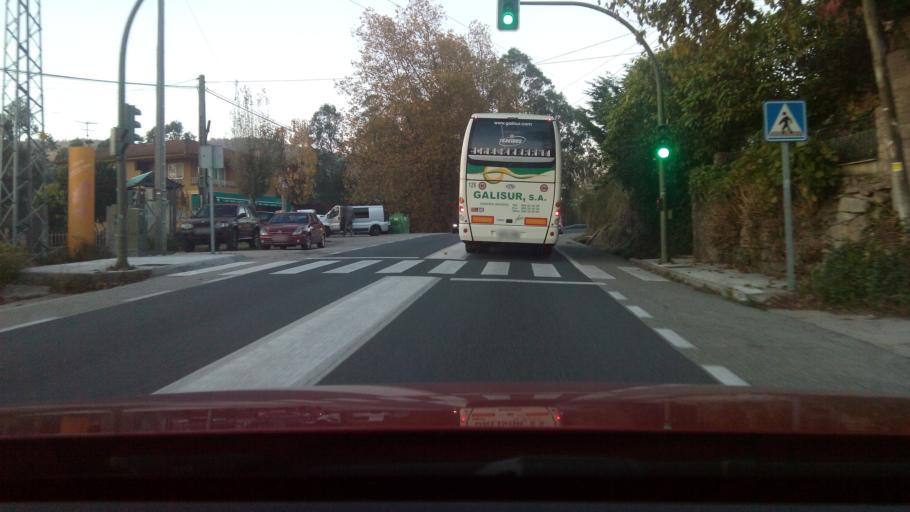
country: ES
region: Galicia
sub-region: Provincia de Pontevedra
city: Gondomar
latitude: 42.1504
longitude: -8.7263
